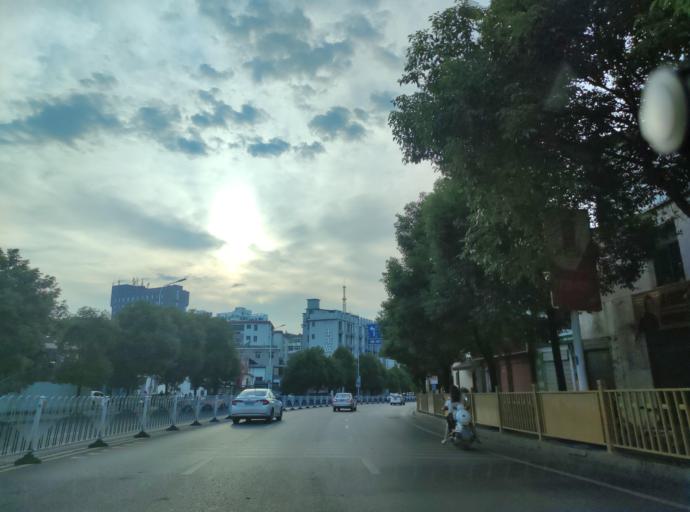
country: CN
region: Jiangxi Sheng
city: Pingxiang
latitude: 27.6338
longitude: 113.8592
